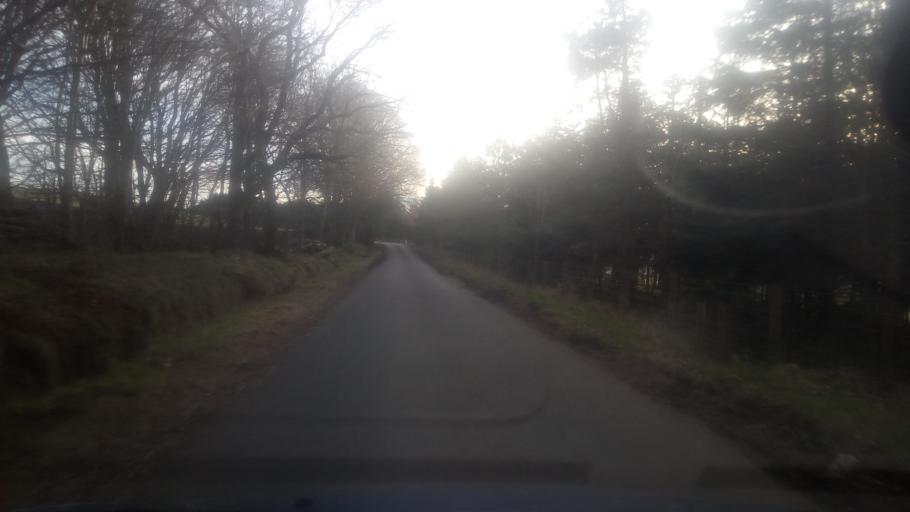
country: GB
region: Scotland
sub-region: The Scottish Borders
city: Jedburgh
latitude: 55.4215
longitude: -2.6181
